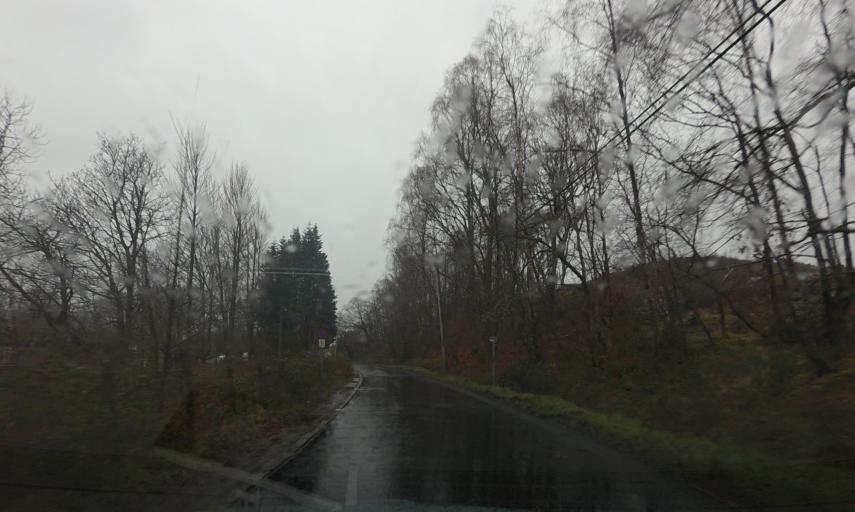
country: GB
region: Scotland
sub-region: West Dunbartonshire
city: Balloch
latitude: 56.1483
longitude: -4.6395
